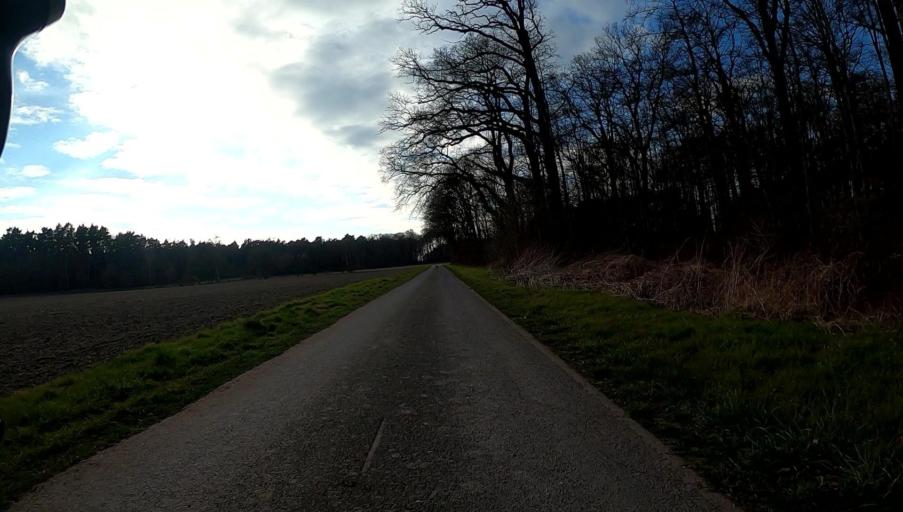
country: DE
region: Lower Saxony
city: Schwarmstedt
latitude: 52.6189
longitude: 9.6159
